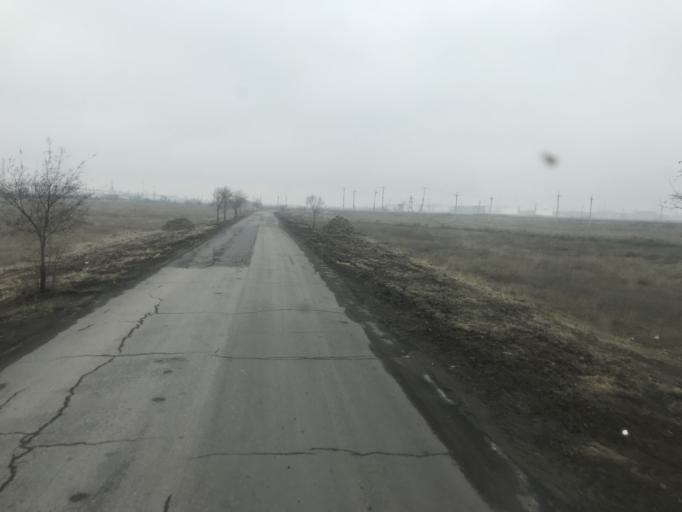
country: RU
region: Volgograd
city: Svetlyy Yar
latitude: 48.4911
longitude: 44.6596
